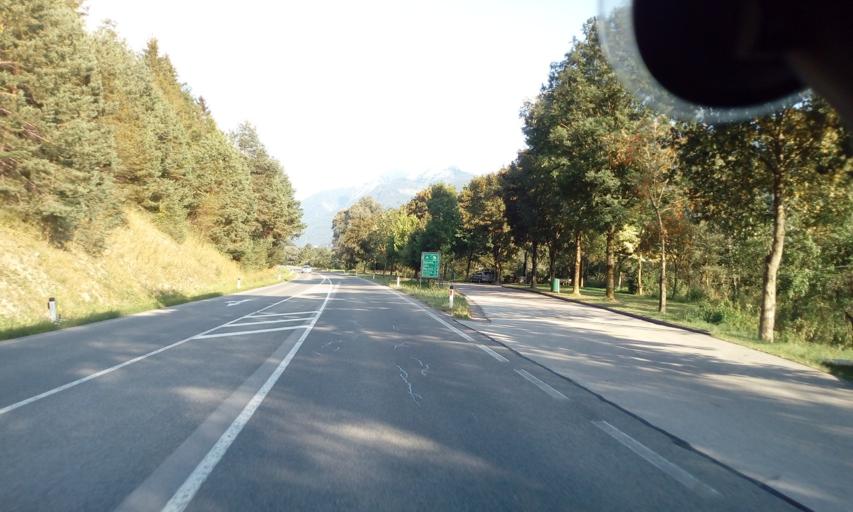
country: AT
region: Carinthia
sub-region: Politischer Bezirk Spittal an der Drau
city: Oberdrauburg
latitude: 46.7552
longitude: 12.9501
